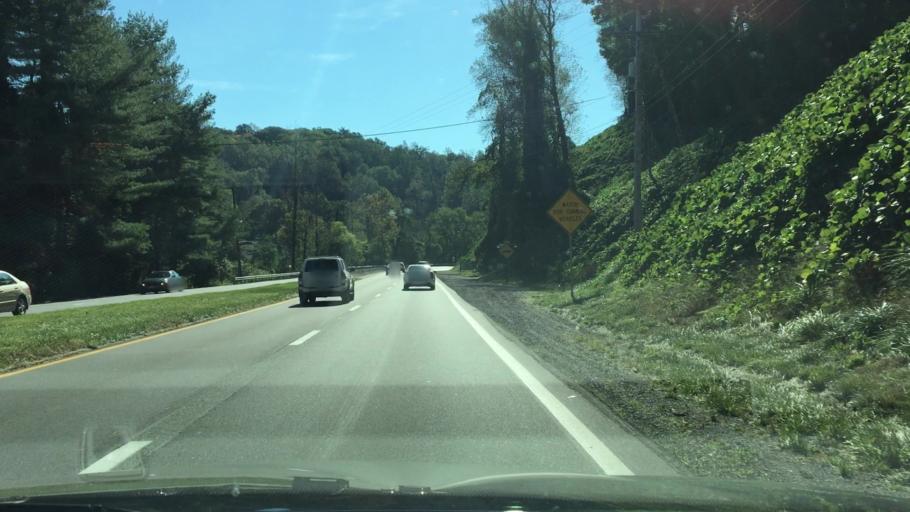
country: US
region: Virginia
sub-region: Roanoke County
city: Narrows
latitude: 37.1232
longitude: -79.9575
